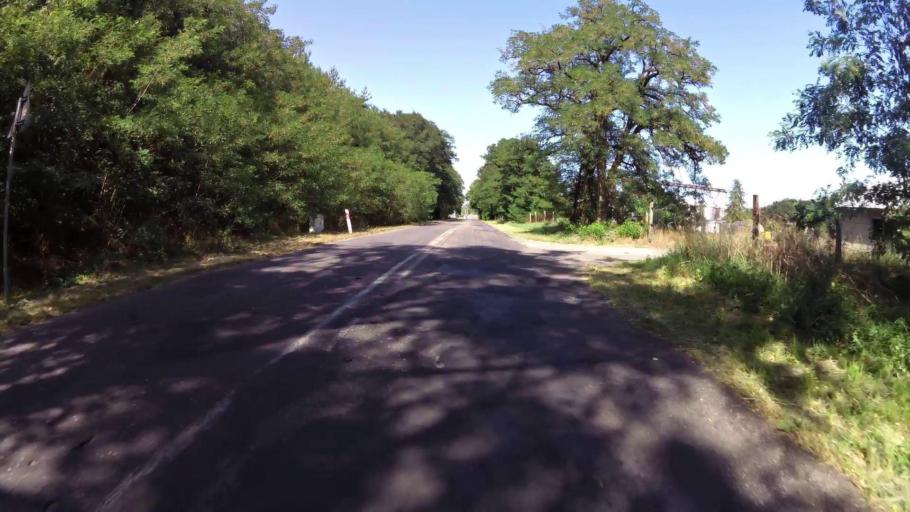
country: PL
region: West Pomeranian Voivodeship
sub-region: Powiat stargardzki
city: Dobrzany
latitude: 53.3361
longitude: 15.3935
